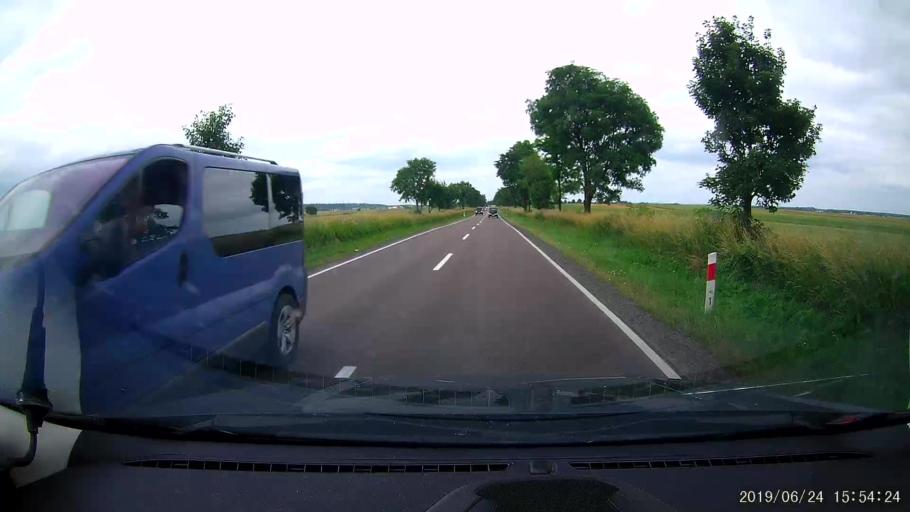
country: PL
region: Subcarpathian Voivodeship
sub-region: Powiat lubaczowski
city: Cieszanow
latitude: 50.2193
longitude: 23.1142
